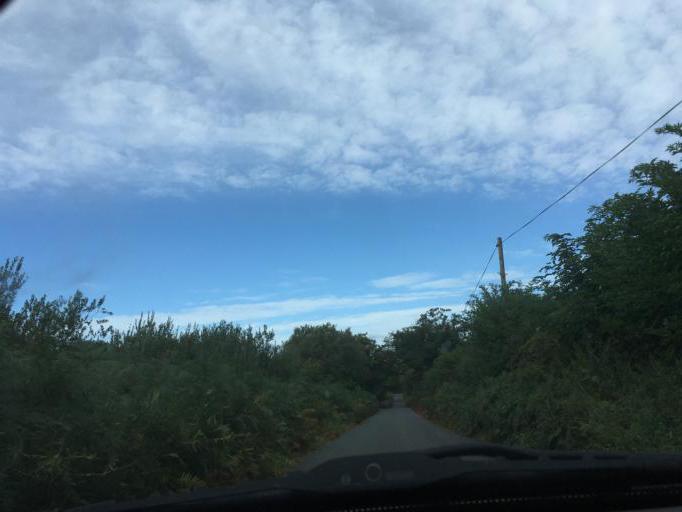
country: IE
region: Leinster
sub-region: Wicklow
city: Rathnew
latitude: 52.9231
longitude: -6.1096
